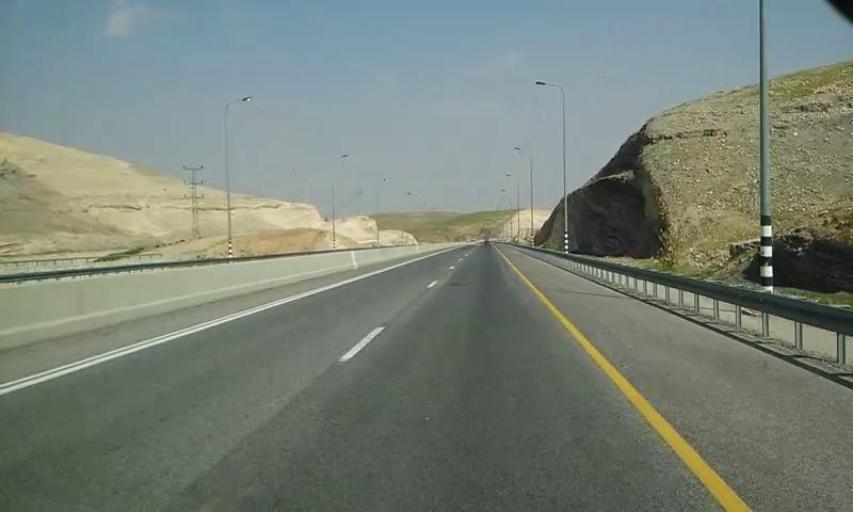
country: PS
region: West Bank
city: Jericho
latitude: 31.8200
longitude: 35.3801
